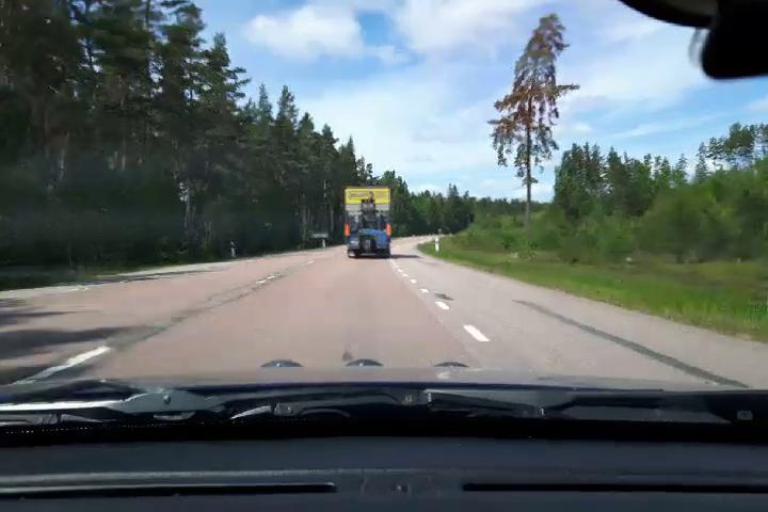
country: SE
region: Uppsala
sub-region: Osthammars Kommun
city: Bjorklinge
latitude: 60.1212
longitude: 17.5109
